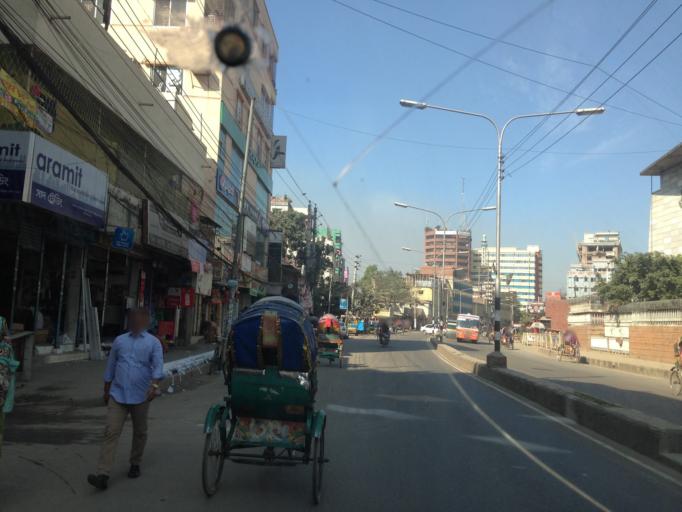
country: BD
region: Dhaka
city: Azimpur
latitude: 23.8070
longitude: 90.3621
